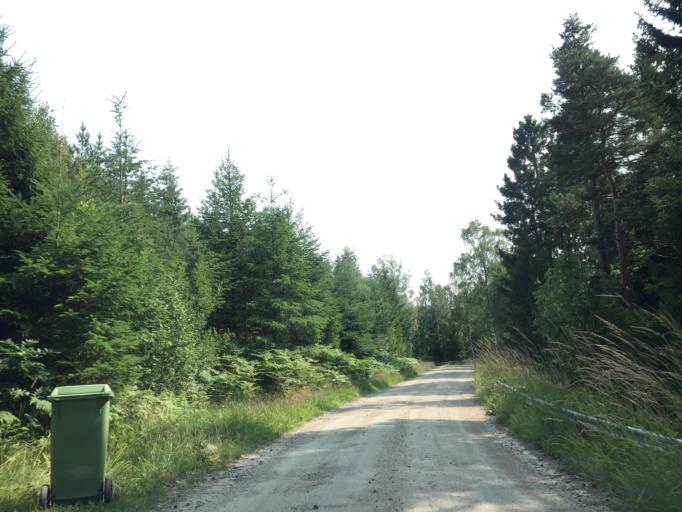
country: SE
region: Vaestra Goetaland
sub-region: Lilla Edets Kommun
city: Lilla Edet
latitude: 58.2398
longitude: 12.0779
